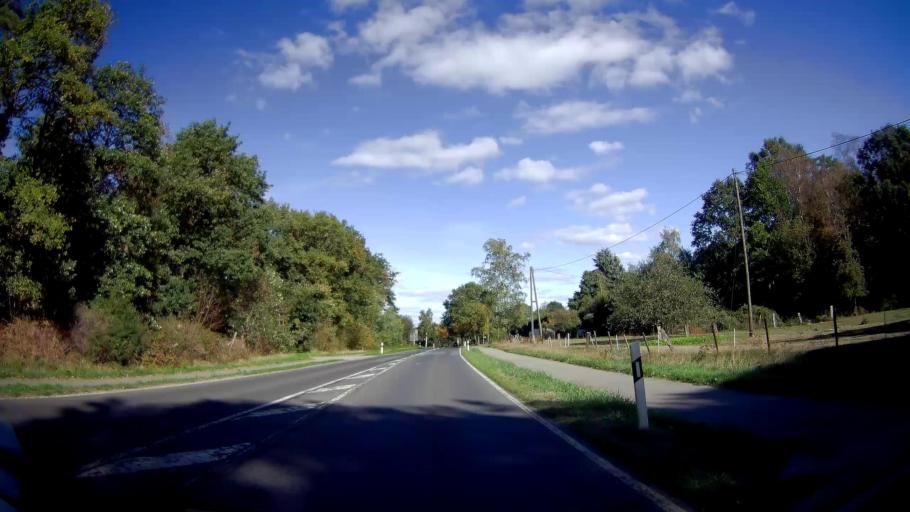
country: DE
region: North Rhine-Westphalia
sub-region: Regierungsbezirk Dusseldorf
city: Hunxe
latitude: 51.6295
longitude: 6.7592
